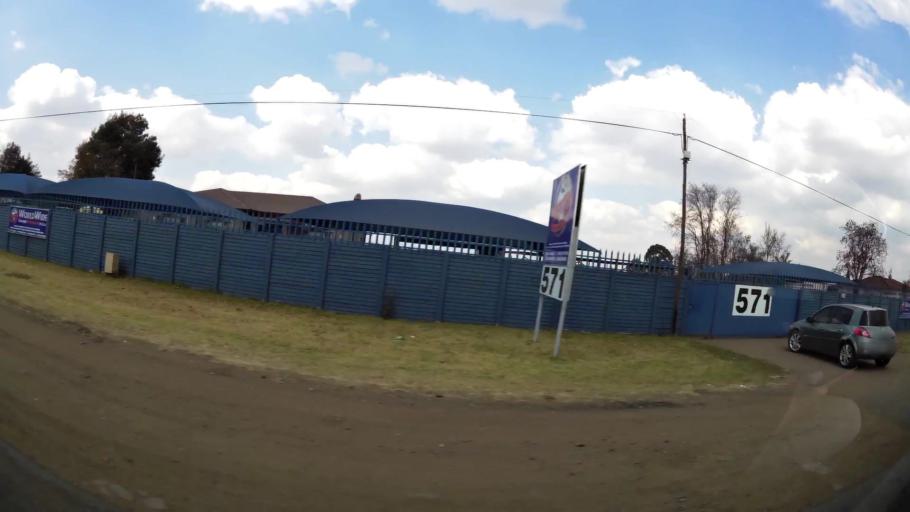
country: ZA
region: Gauteng
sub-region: Ekurhuleni Metropolitan Municipality
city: Benoni
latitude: -26.1116
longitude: 28.3654
